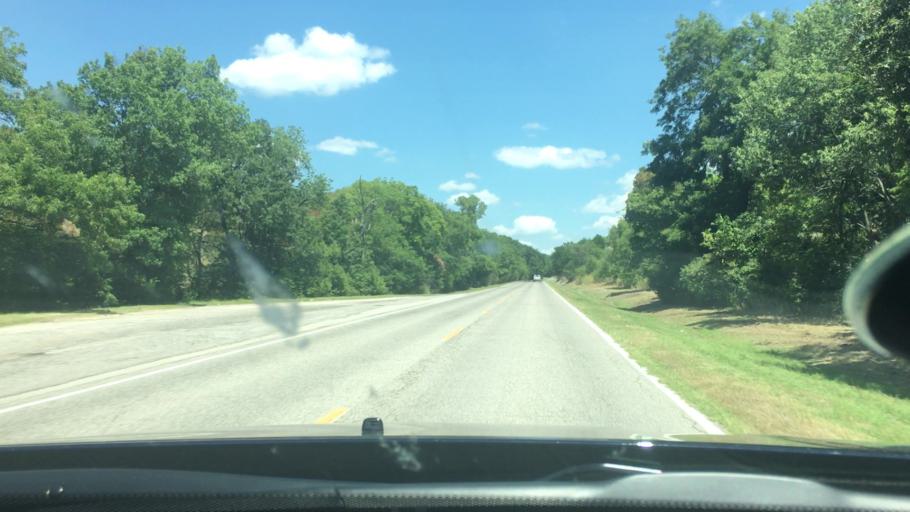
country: US
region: Oklahoma
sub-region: Carter County
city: Dickson
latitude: 34.3107
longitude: -96.9626
